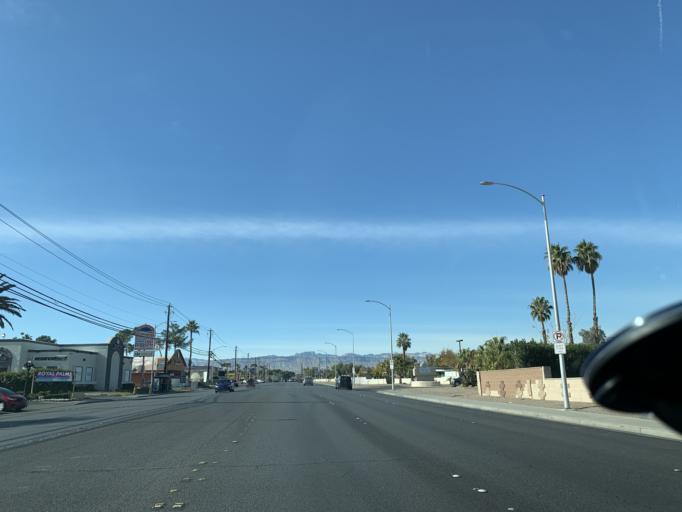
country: US
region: Nevada
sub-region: Clark County
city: Spring Valley
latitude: 36.1003
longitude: -115.2191
